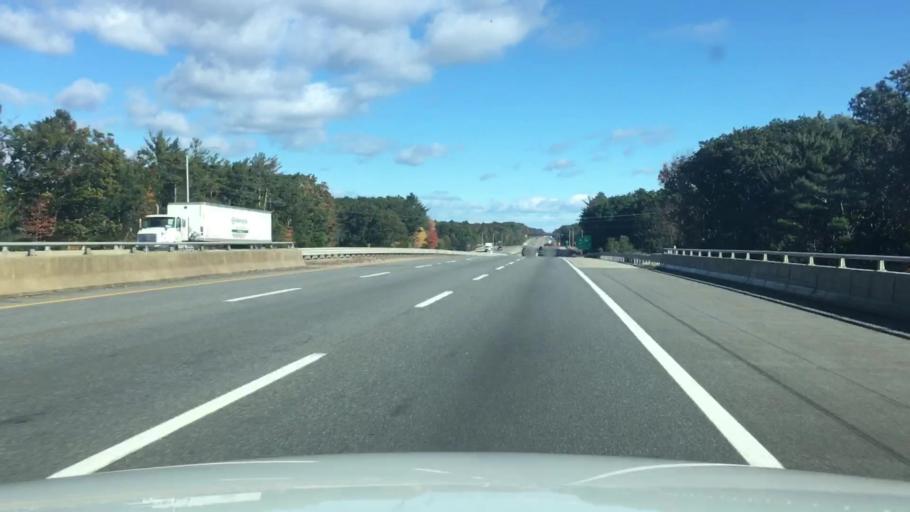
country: US
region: Maine
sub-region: York County
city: Wells Beach Station
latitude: 43.3208
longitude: -70.6093
